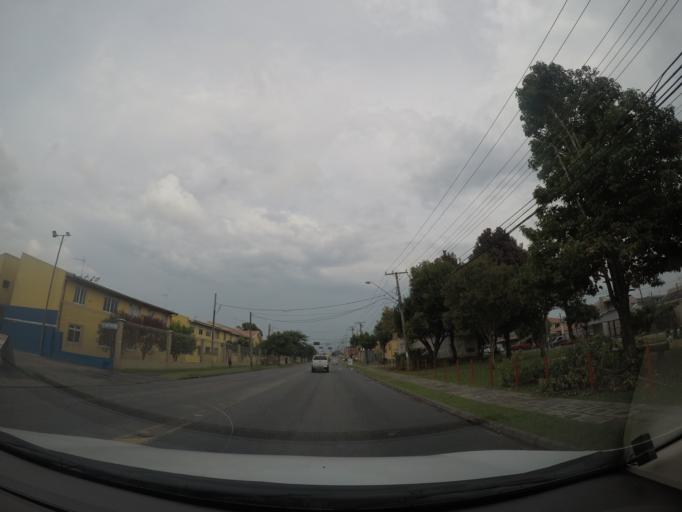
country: BR
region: Parana
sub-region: Sao Jose Dos Pinhais
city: Sao Jose dos Pinhais
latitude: -25.5298
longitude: -49.2595
